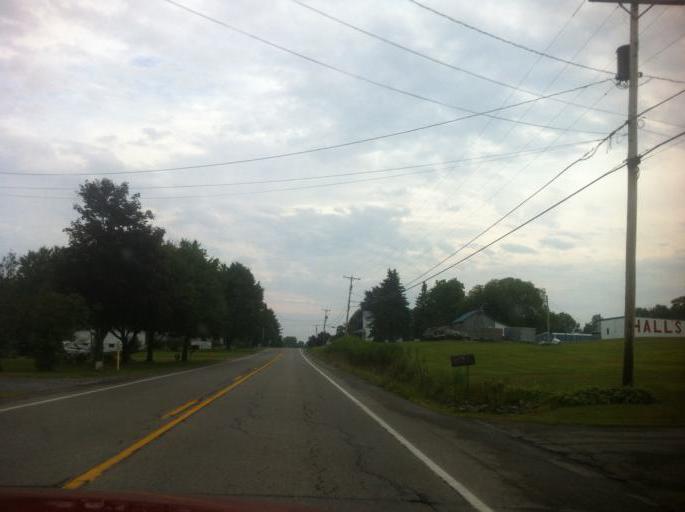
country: US
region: Pennsylvania
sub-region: Mercer County
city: Grove City
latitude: 41.1832
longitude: -80.0841
